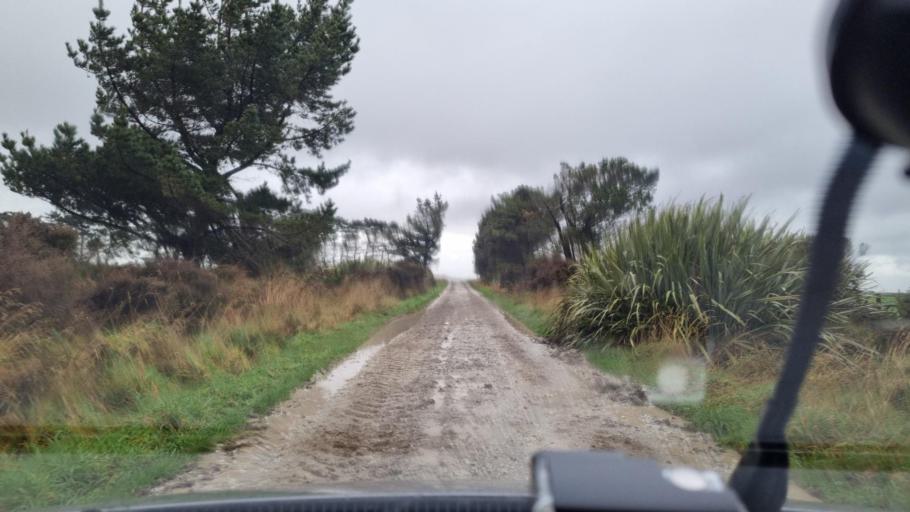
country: NZ
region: Southland
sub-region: Invercargill City
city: Bluff
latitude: -46.5683
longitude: 168.5010
